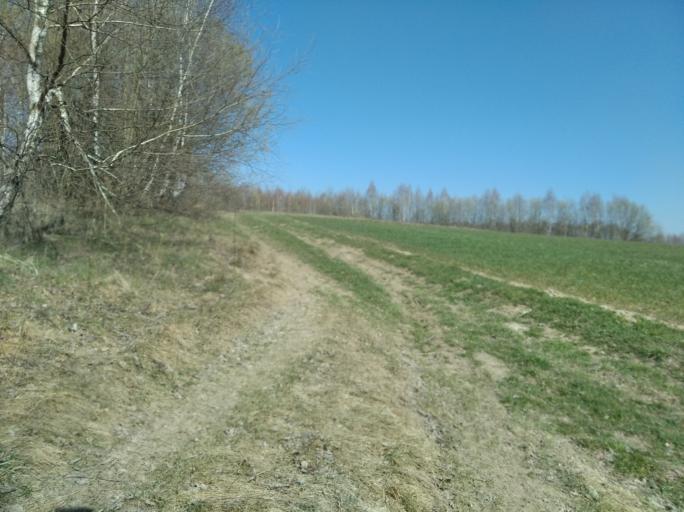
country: PL
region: Subcarpathian Voivodeship
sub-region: Powiat strzyzowski
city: Jawornik
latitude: 49.8514
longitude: 21.8542
